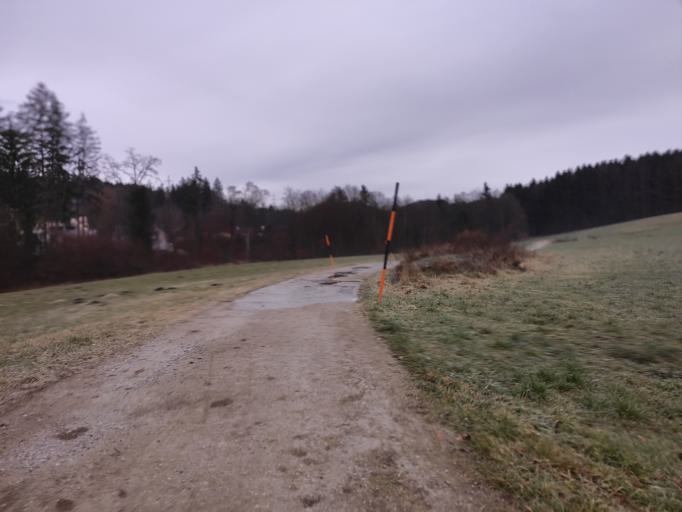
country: AT
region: Salzburg
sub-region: Politischer Bezirk Salzburg-Umgebung
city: Elixhausen
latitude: 47.8592
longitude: 13.0534
